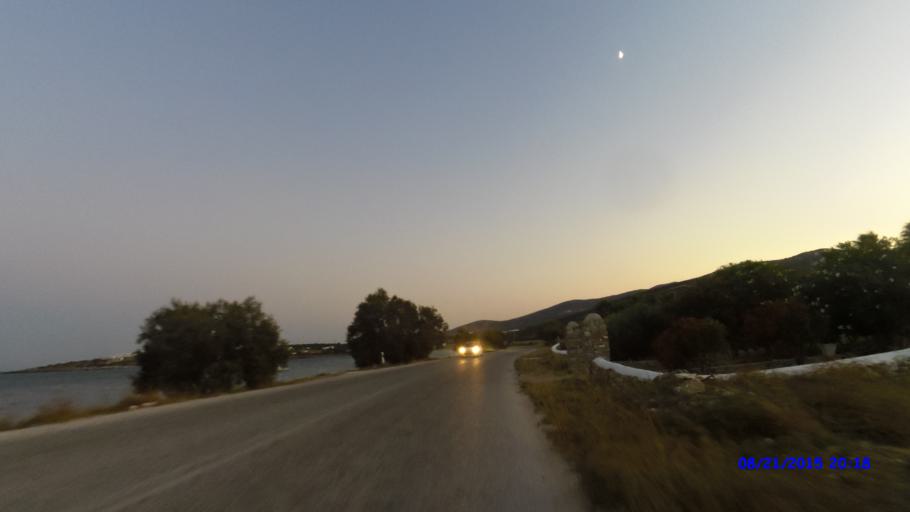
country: GR
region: South Aegean
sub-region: Nomos Kykladon
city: Antiparos
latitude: 37.0089
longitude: 25.0746
